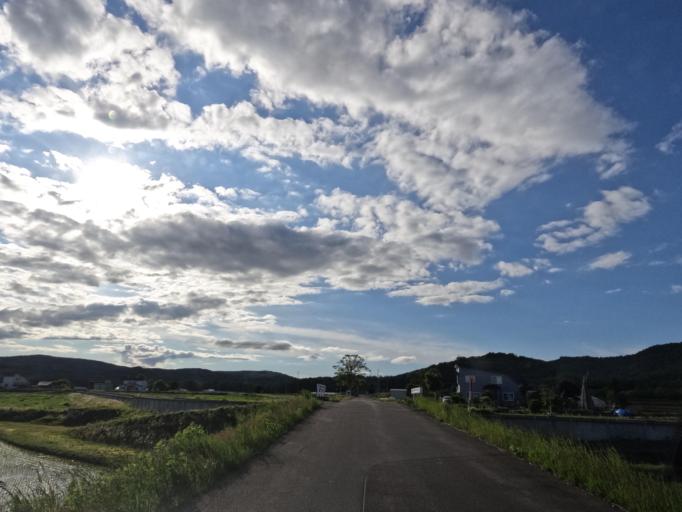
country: JP
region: Hokkaido
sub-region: Asahikawa-shi
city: Asahikawa
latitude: 43.9178
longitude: 142.4946
